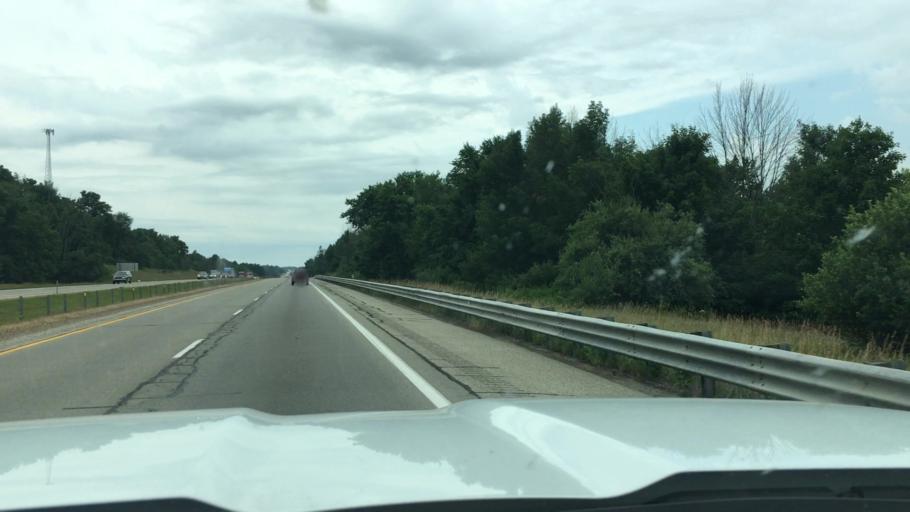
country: US
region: Michigan
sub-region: Allegan County
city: Wayland
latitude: 42.5799
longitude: -85.6628
